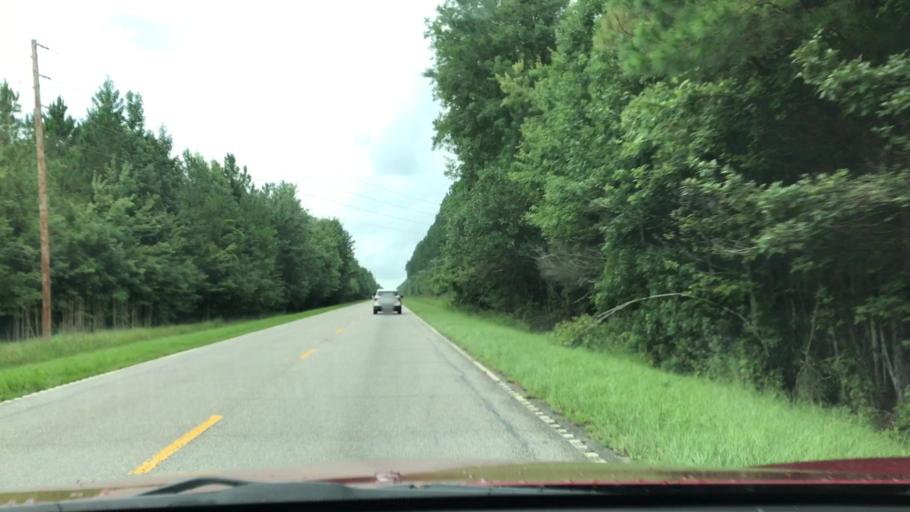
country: US
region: South Carolina
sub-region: Georgetown County
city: Murrells Inlet
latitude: 33.6005
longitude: -79.2006
